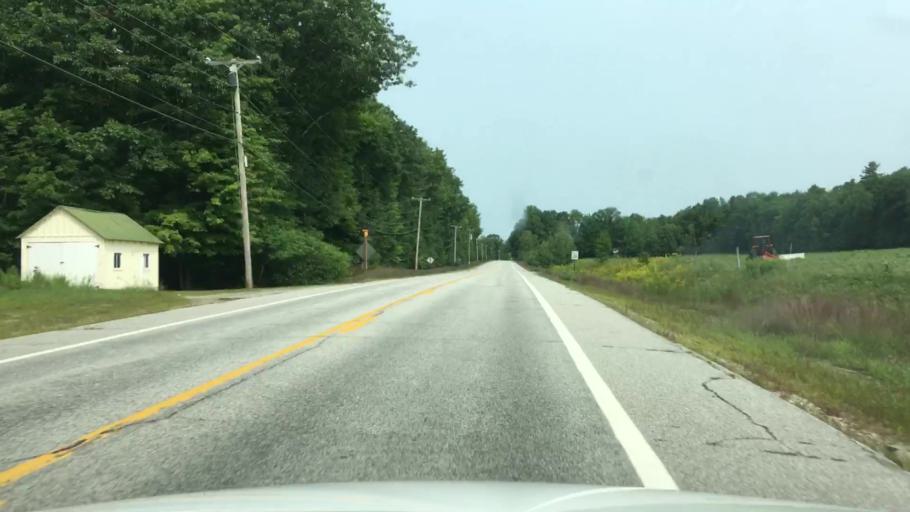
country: US
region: Maine
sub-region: Androscoggin County
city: Livermore Falls
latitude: 44.4237
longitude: -70.1445
